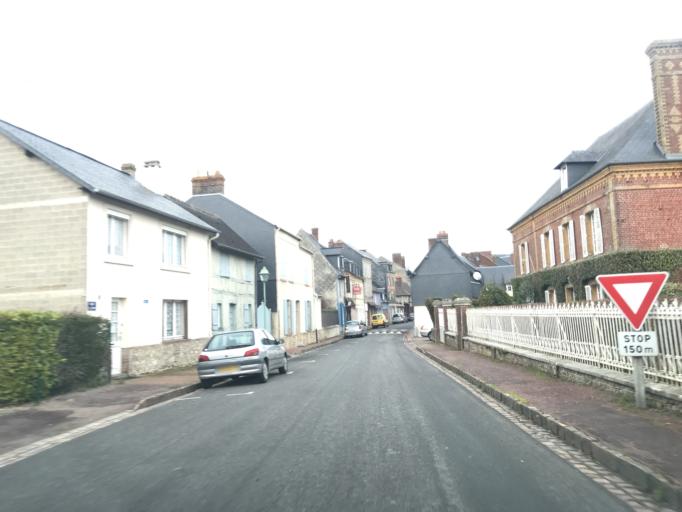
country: FR
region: Lower Normandy
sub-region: Departement du Calvados
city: Touques
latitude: 49.2771
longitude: 0.1090
